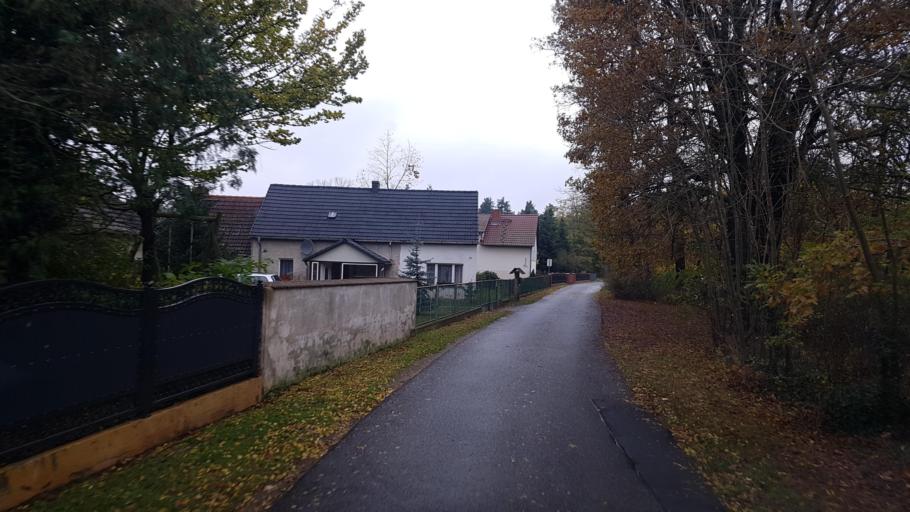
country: DE
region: Brandenburg
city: Drebkau
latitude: 51.6977
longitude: 14.1941
